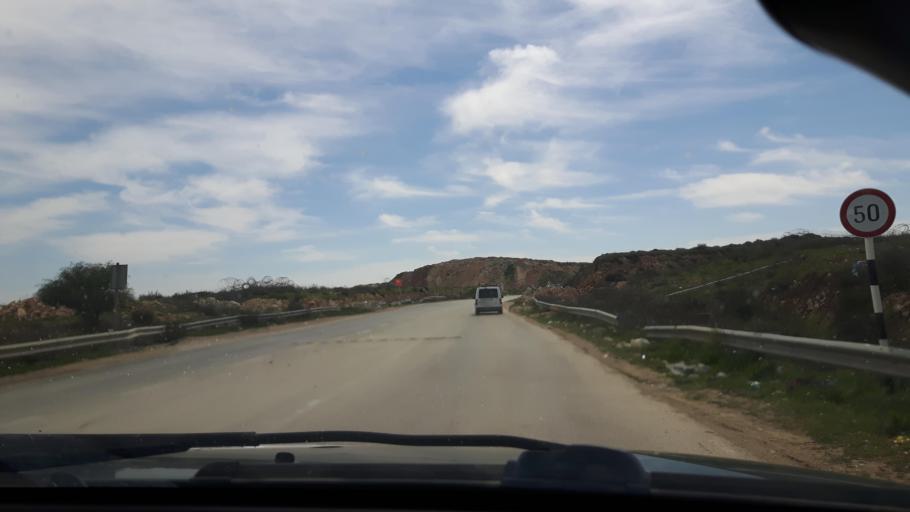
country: PS
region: West Bank
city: Rafat
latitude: 31.8737
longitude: 35.1992
